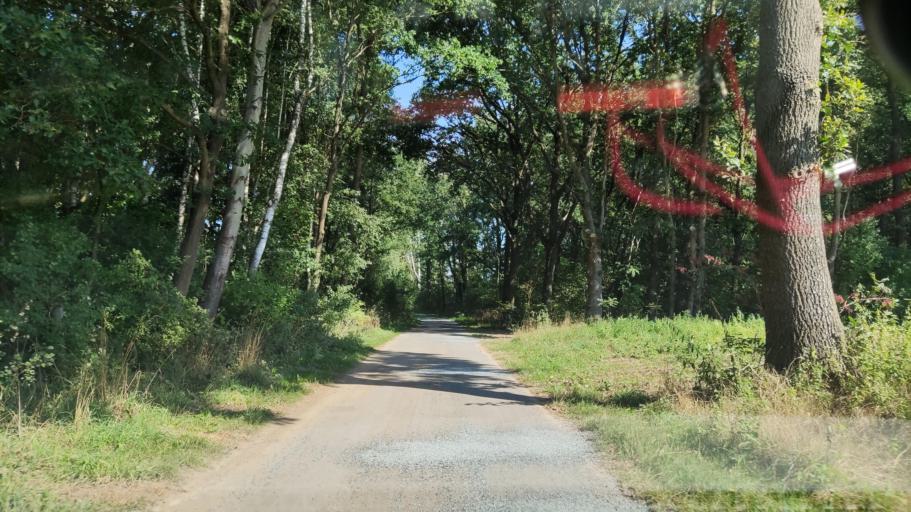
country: DE
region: Lower Saxony
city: Hitzacker
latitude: 53.1442
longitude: 10.9765
